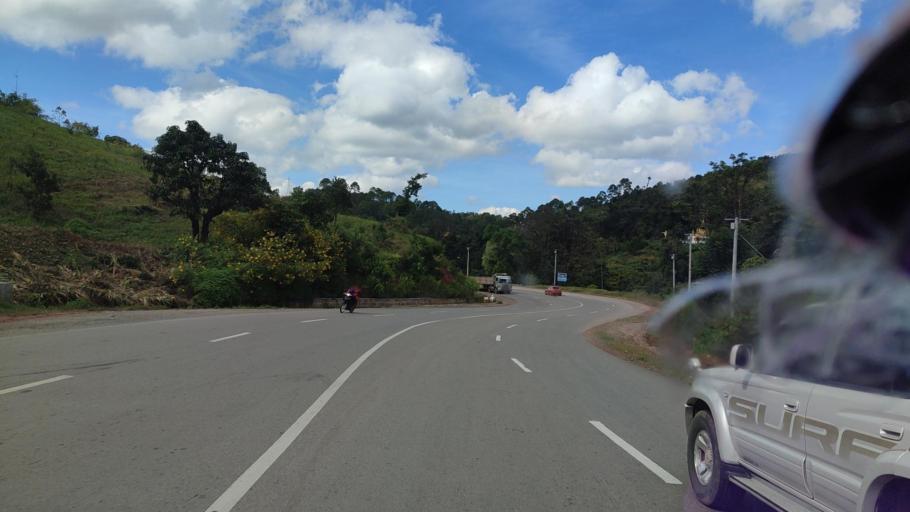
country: MM
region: Mandalay
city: Yamethin
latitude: 20.6579
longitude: 96.5429
